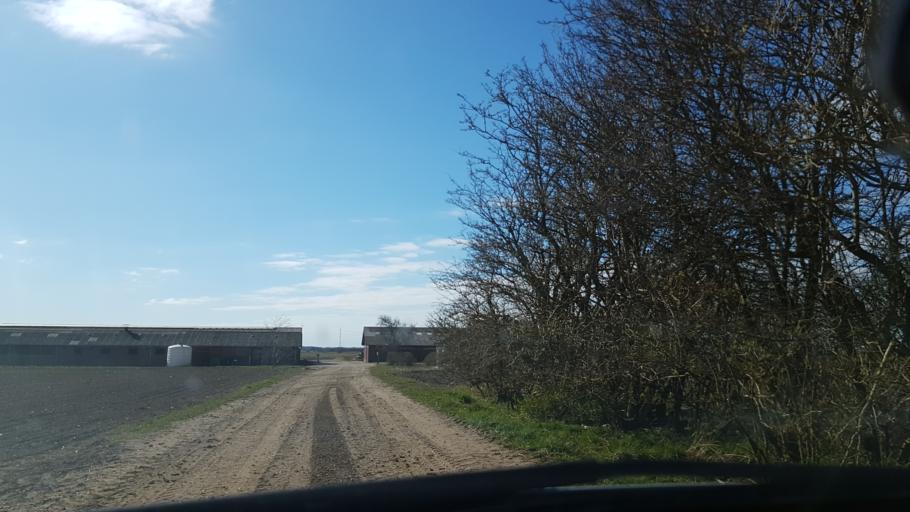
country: DK
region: South Denmark
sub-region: Tonder Kommune
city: Sherrebek
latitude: 55.2397
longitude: 8.8284
